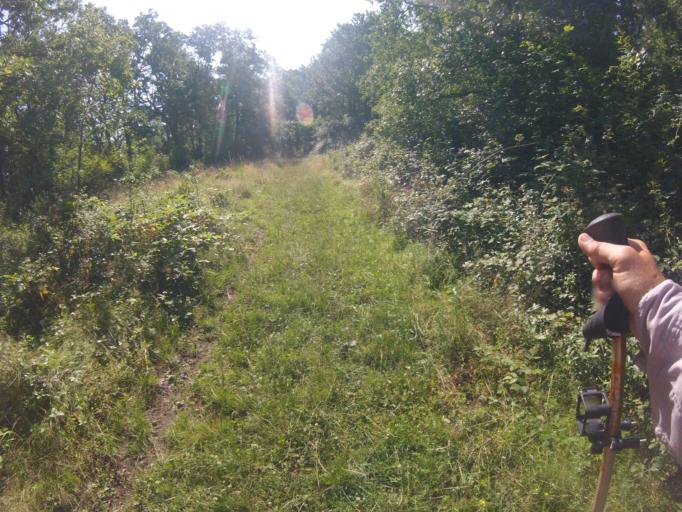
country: SK
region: Nitriansky
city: Sahy
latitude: 47.9909
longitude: 18.8867
